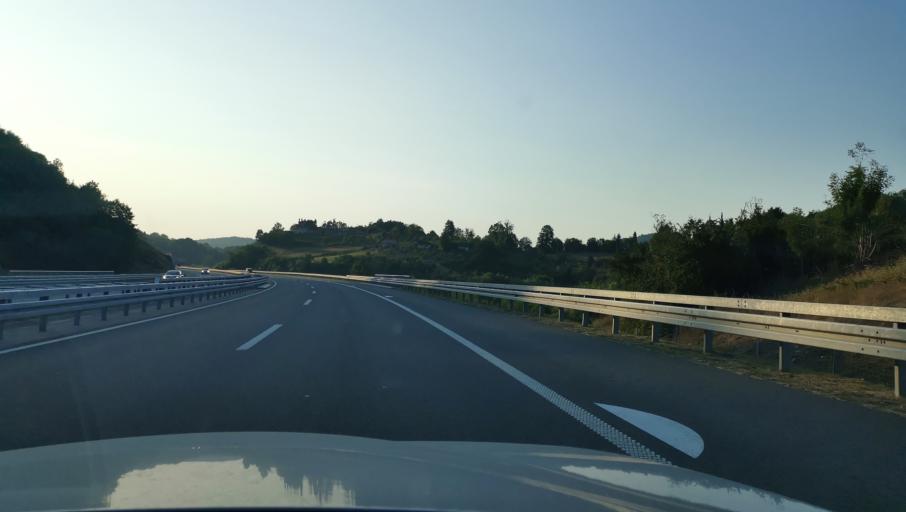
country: RS
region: Central Serbia
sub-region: Kolubarski Okrug
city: Ljig
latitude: 44.1891
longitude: 20.2931
